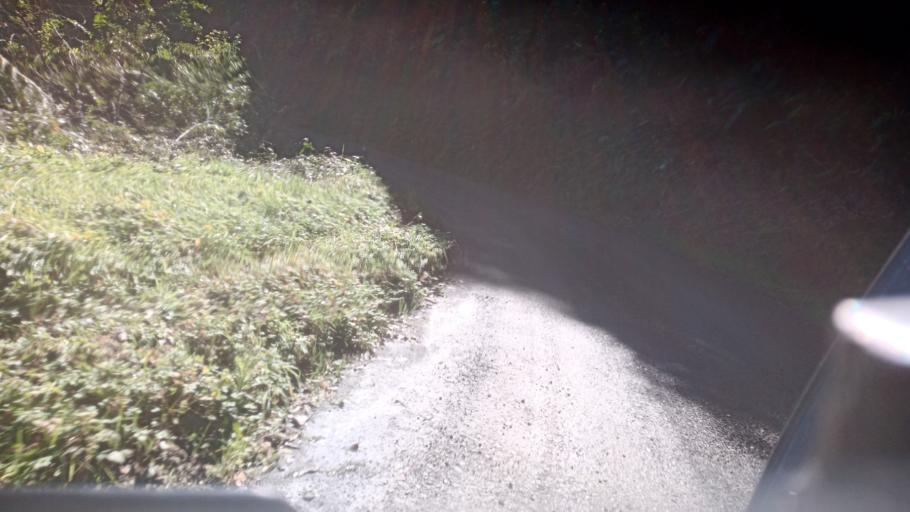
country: NZ
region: Bay of Plenty
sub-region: Opotiki District
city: Opotiki
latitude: -38.0523
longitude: 177.4572
